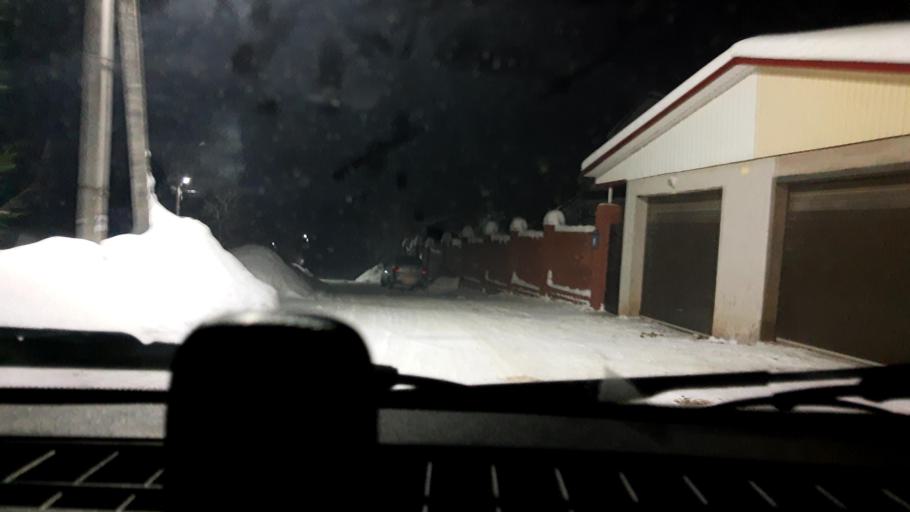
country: RU
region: Bashkortostan
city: Avdon
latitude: 54.6215
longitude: 55.6372
